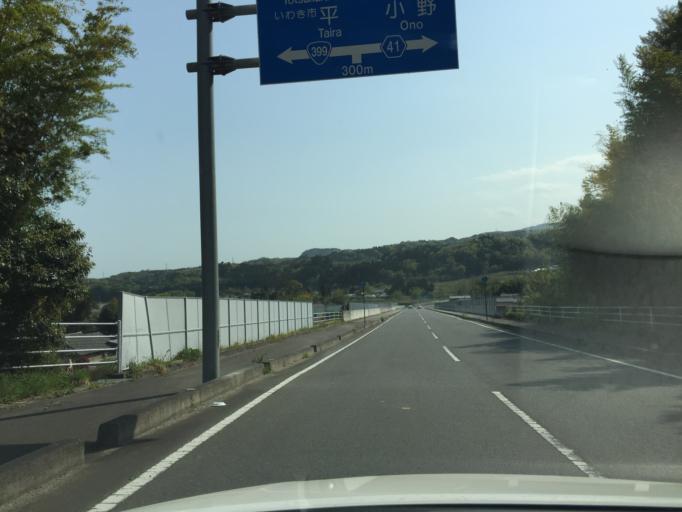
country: JP
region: Fukushima
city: Iwaki
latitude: 37.1371
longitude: 140.8542
